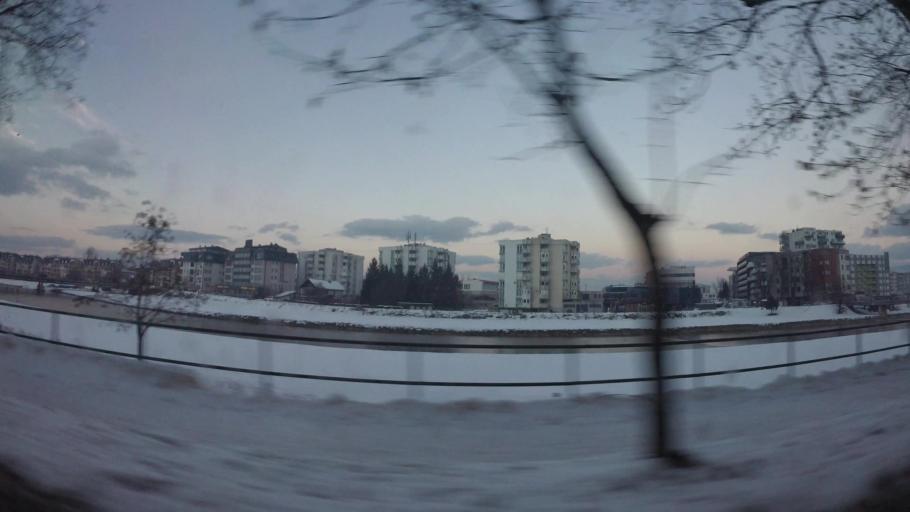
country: BA
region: Federation of Bosnia and Herzegovina
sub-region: Kanton Sarajevo
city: Sarajevo
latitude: 43.8285
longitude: 18.3058
